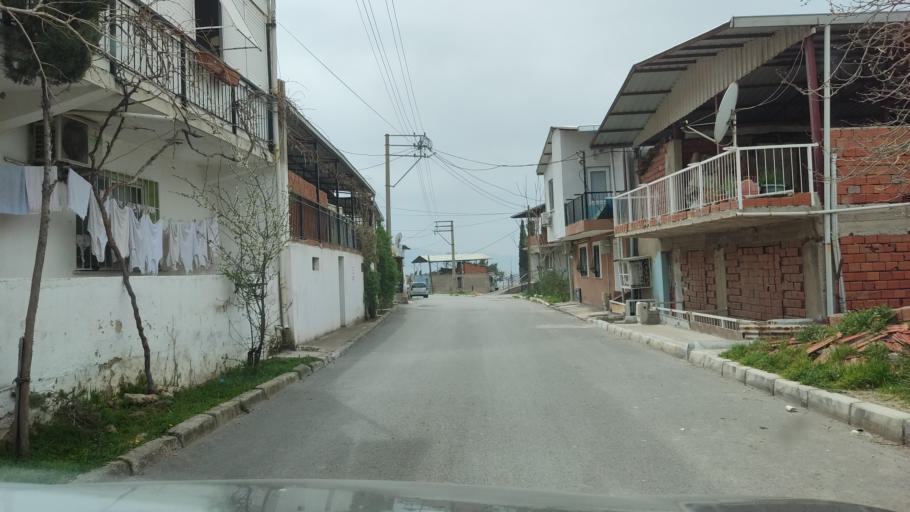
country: TR
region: Izmir
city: Karsiyaka
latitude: 38.4999
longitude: 27.0725
